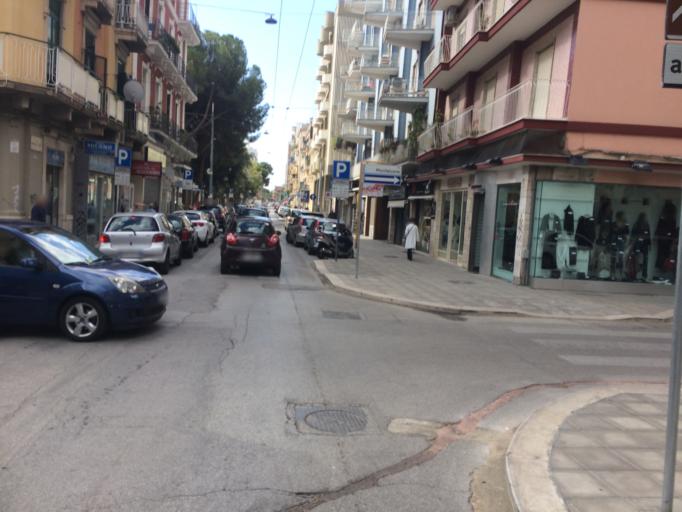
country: IT
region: Apulia
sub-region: Provincia di Bari
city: Bari
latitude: 41.1110
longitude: 16.8721
